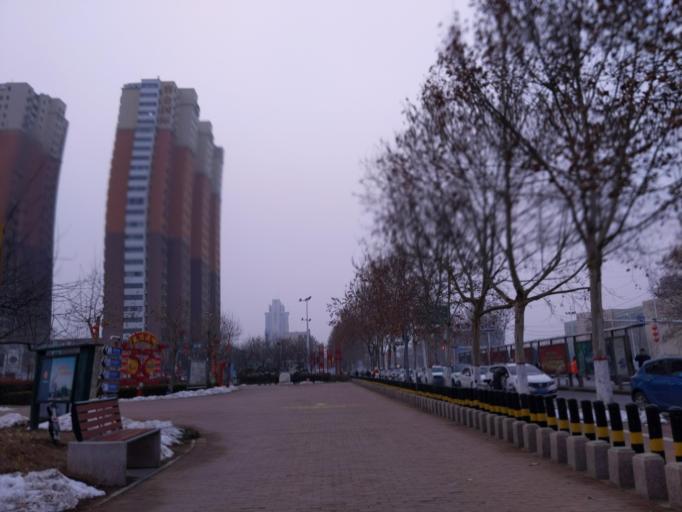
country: CN
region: Henan Sheng
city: Puyang
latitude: 35.7807
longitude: 115.0276
